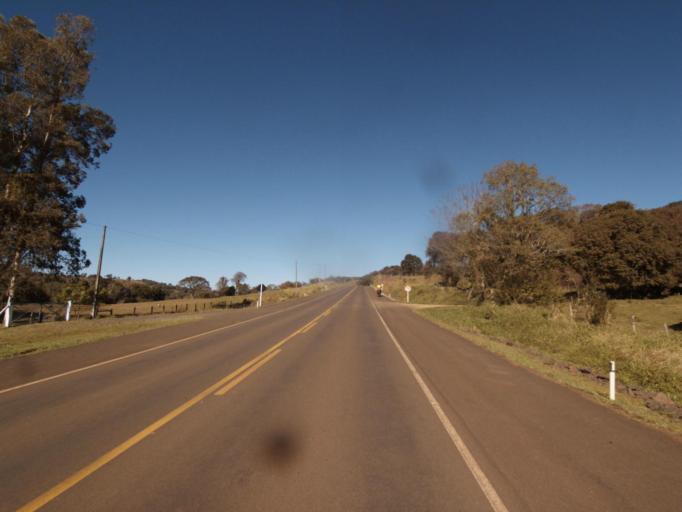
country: AR
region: Misiones
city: Bernardo de Irigoyen
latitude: -26.6888
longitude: -53.5479
